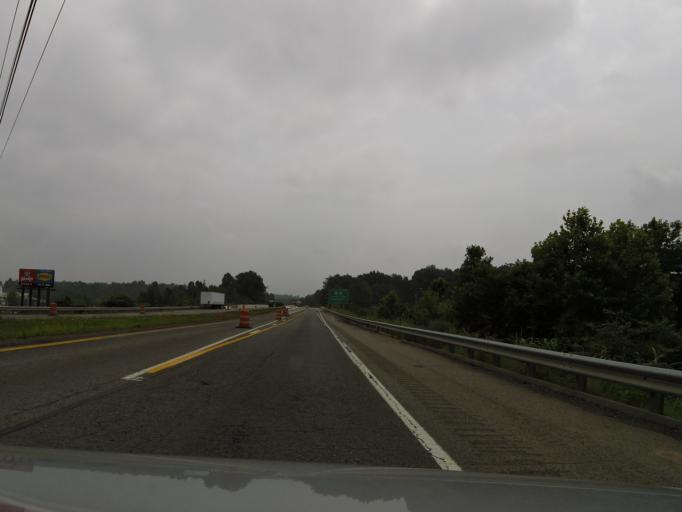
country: US
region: Kentucky
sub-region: Muhlenberg County
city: Central City
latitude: 37.2739
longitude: -87.1450
